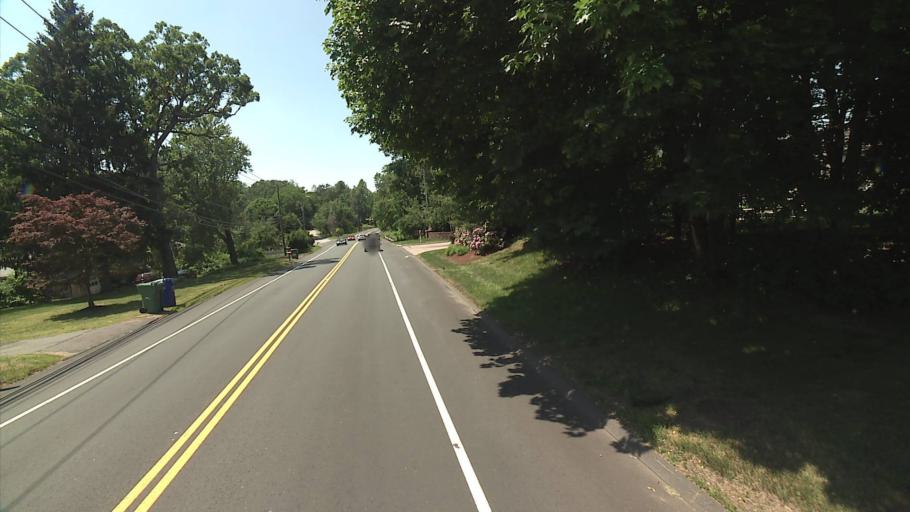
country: US
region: Connecticut
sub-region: Hartford County
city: Manchester
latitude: 41.8149
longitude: -72.5302
